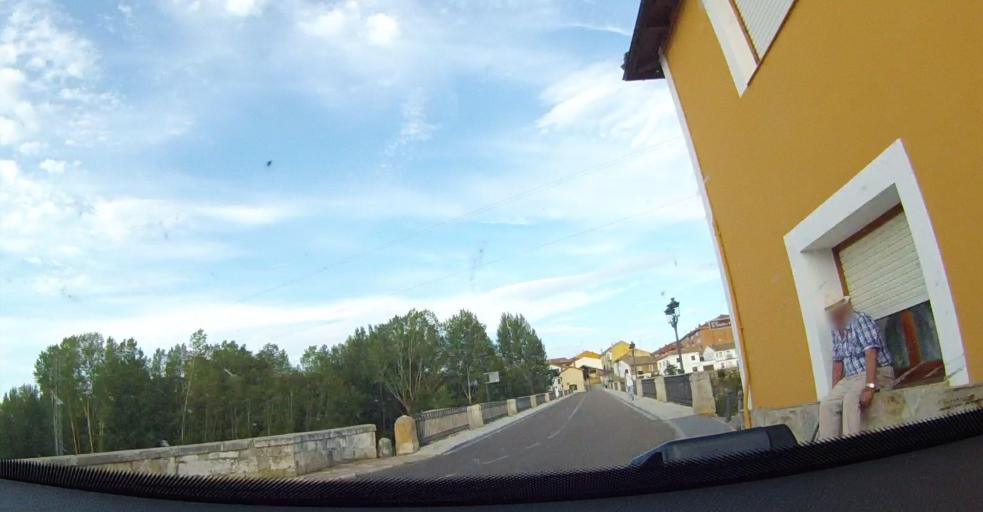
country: ES
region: Castille and Leon
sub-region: Provincia de Palencia
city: Carrion de los Condes
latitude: 42.3396
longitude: -4.6084
